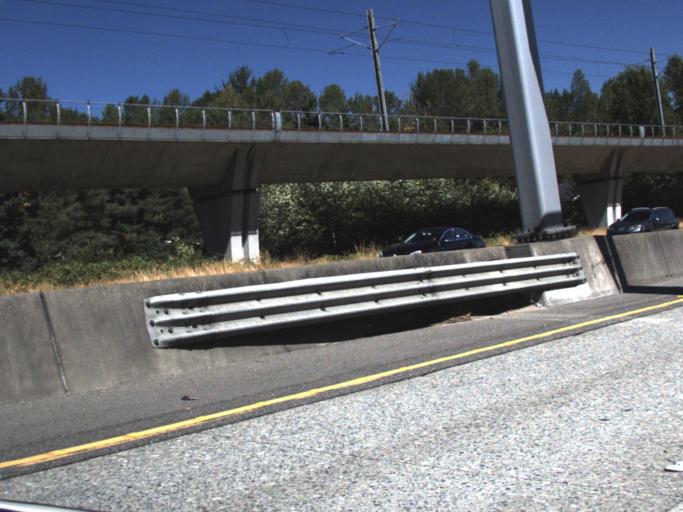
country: US
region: Washington
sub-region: King County
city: Tukwila
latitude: 47.4657
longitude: -122.2771
